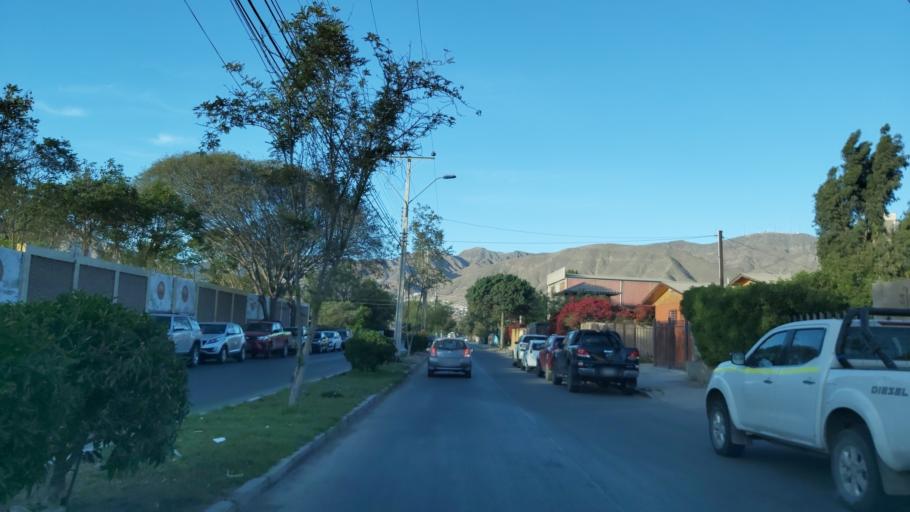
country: CL
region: Atacama
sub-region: Provincia de Copiapo
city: Copiapo
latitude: -27.3779
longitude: -70.3183
